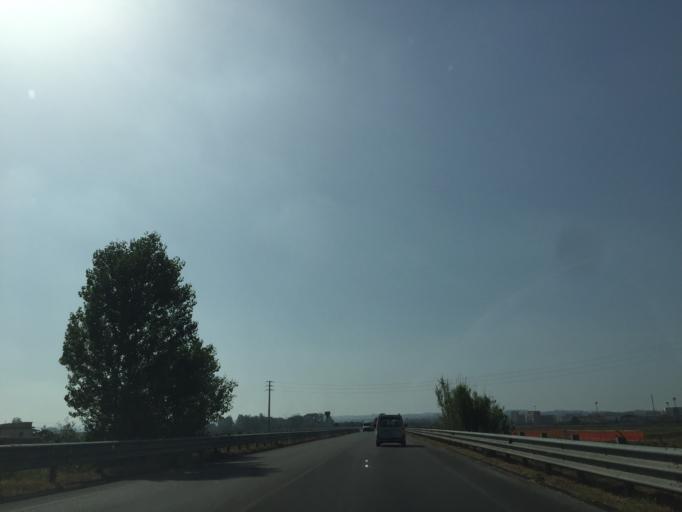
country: IT
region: Tuscany
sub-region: Province of Pisa
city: Pontedera
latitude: 43.6746
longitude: 10.6457
